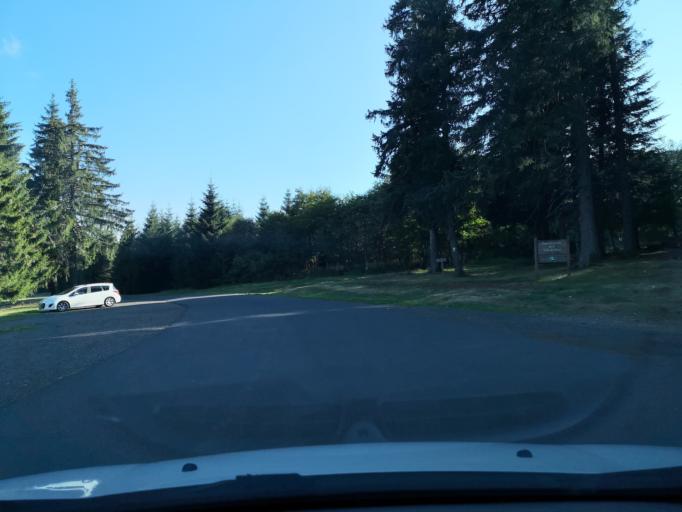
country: FR
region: Auvergne
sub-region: Departement du Puy-de-Dome
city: Mont-Dore
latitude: 45.4926
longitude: 2.8928
